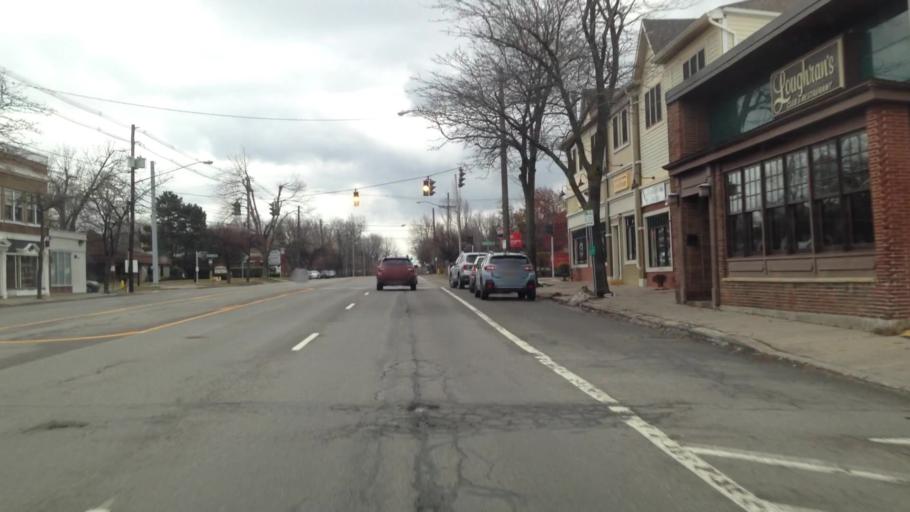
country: US
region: New York
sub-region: Erie County
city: Eggertsville
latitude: 42.9628
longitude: -78.7823
